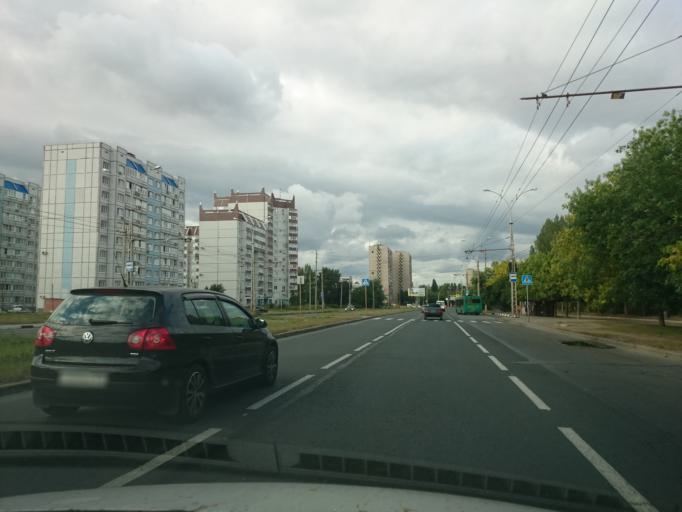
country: RU
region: Samara
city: Tol'yatti
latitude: 53.5024
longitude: 49.2993
